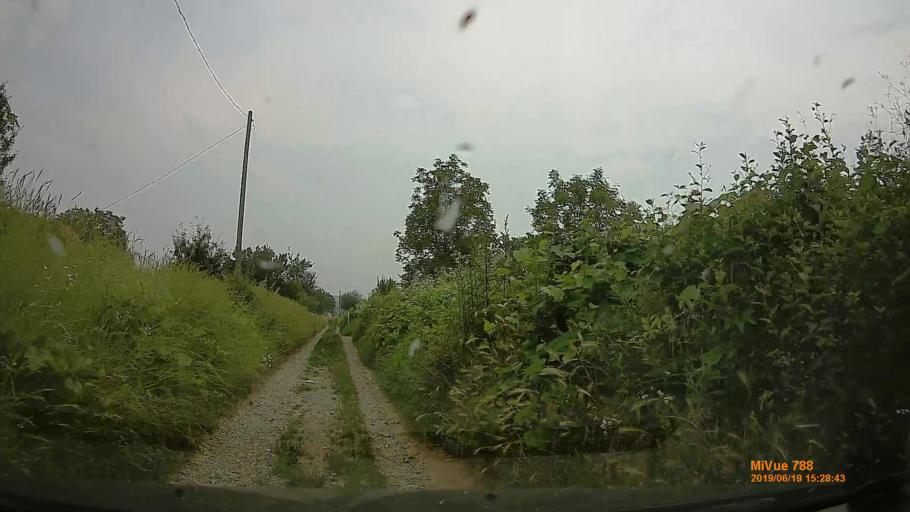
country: HU
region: Baranya
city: Szigetvar
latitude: 46.0705
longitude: 17.8478
